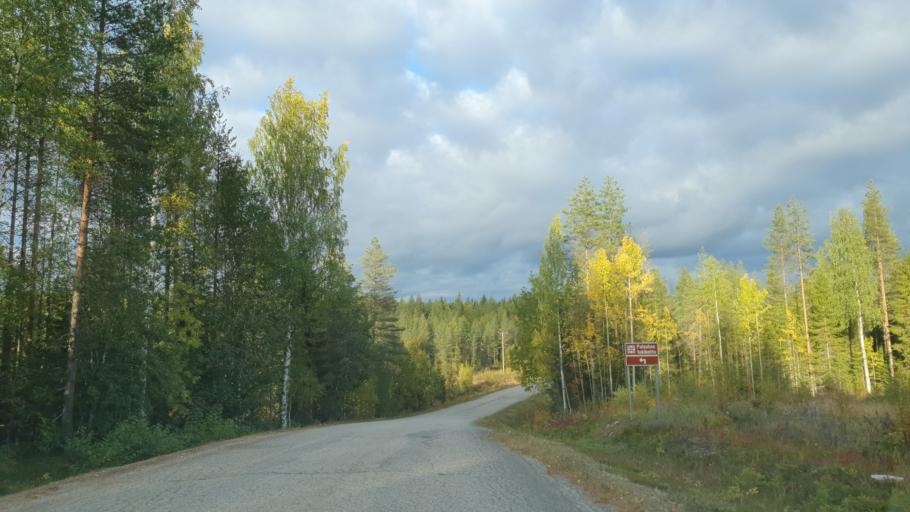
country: FI
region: North Karelia
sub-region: Pielisen Karjala
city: Lieksa
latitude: 63.9197
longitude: 30.1321
